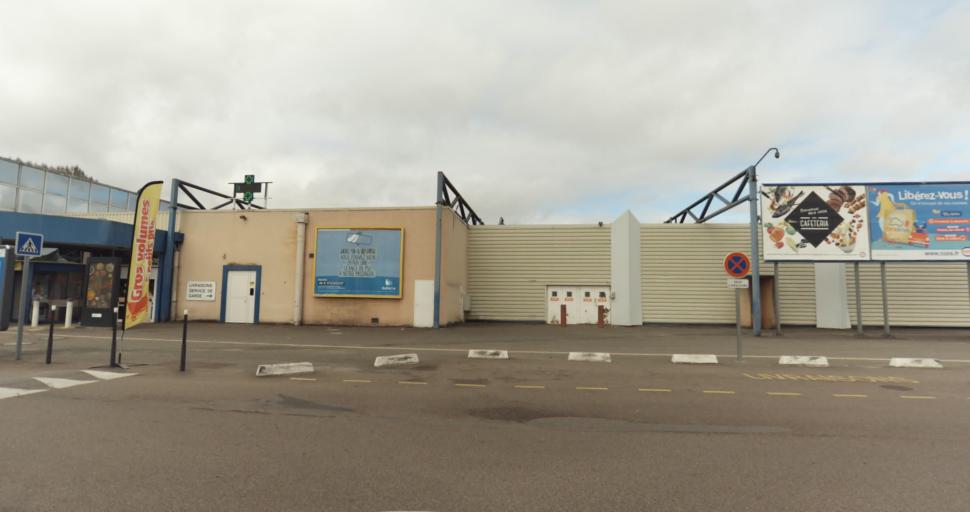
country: FR
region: Haute-Normandie
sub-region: Departement de l'Eure
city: Evreux
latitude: 49.0220
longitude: 1.1349
